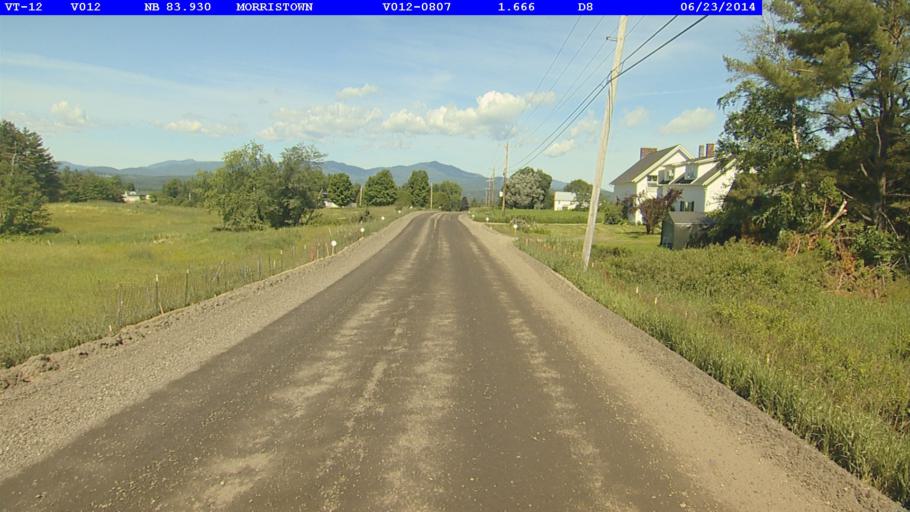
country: US
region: Vermont
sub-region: Lamoille County
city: Morrisville
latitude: 44.5497
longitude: -72.5697
